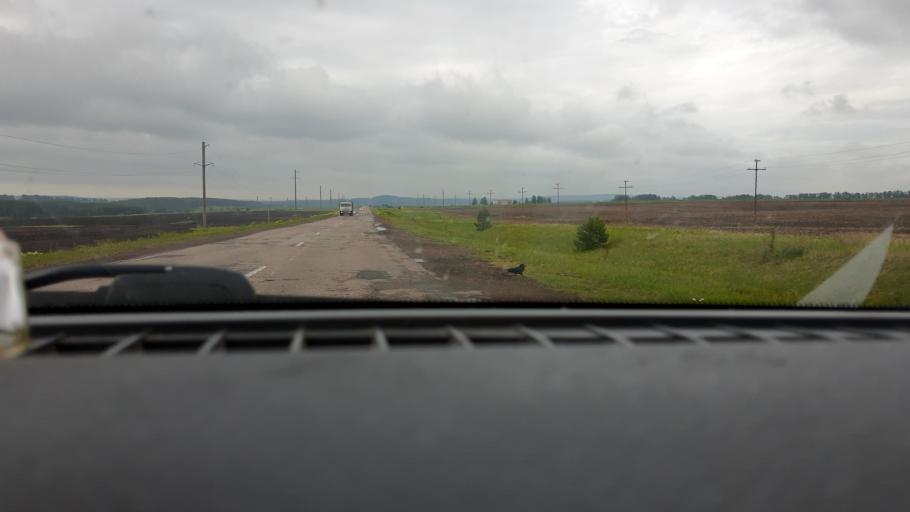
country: RU
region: Bashkortostan
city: Priyutovo
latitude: 53.9615
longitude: 53.9764
